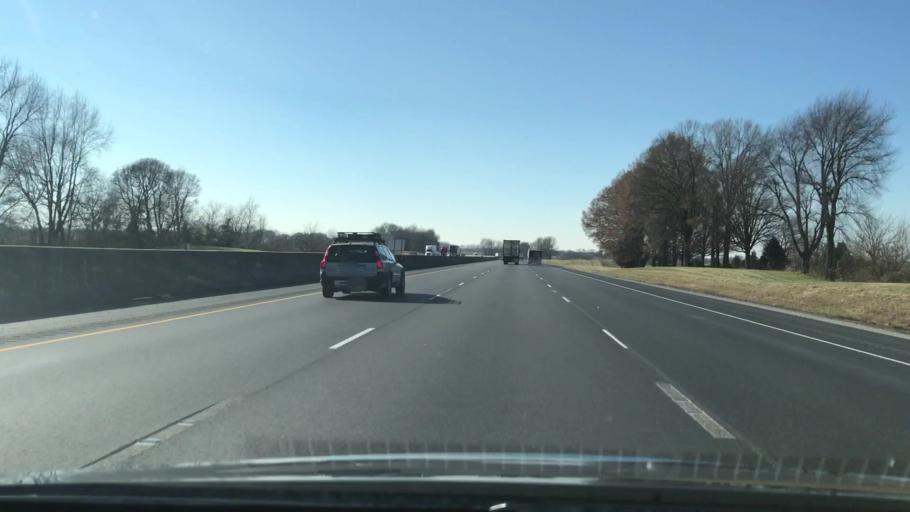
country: US
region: Kentucky
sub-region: Edmonson County
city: Brownsville
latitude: 37.0379
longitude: -86.2271
